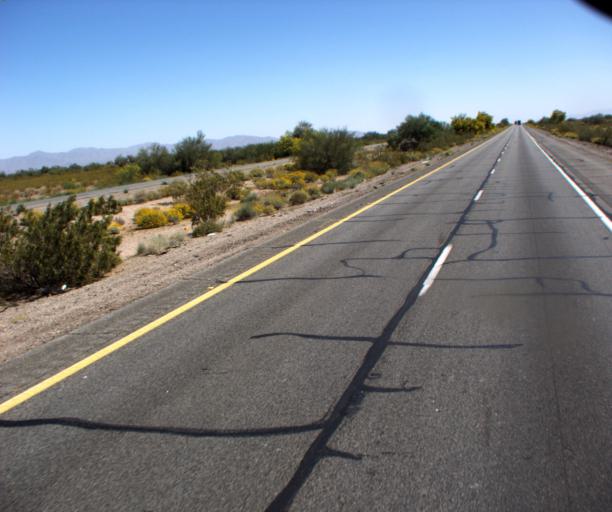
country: US
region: Arizona
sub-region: Maricopa County
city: Buckeye
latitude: 33.4701
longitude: -112.8154
